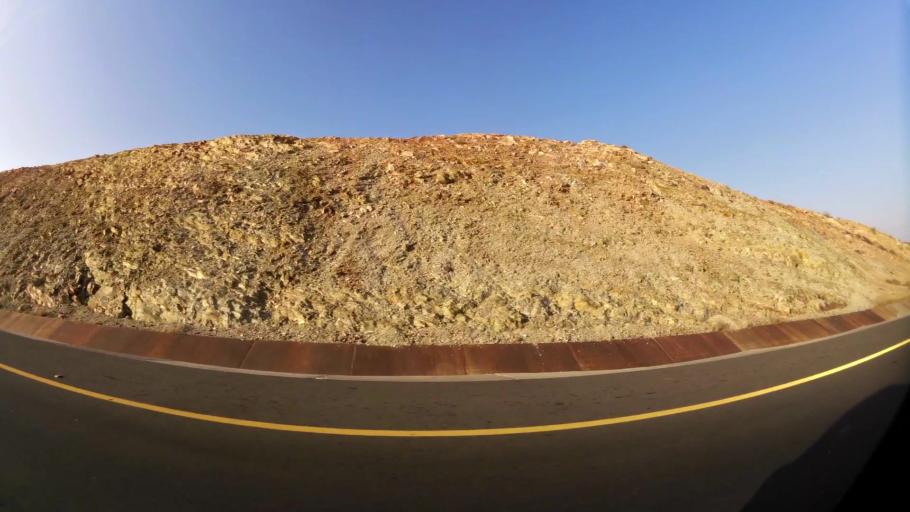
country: ZA
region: Gauteng
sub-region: City of Johannesburg Metropolitan Municipality
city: Roodepoort
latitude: -26.2193
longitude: 27.9404
